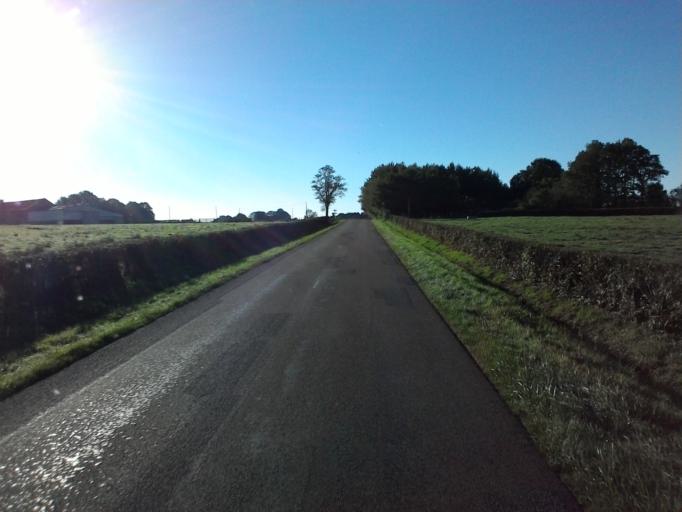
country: FR
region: Bourgogne
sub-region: Departement de la Cote-d'Or
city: Saulieu
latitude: 47.2817
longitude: 4.1899
